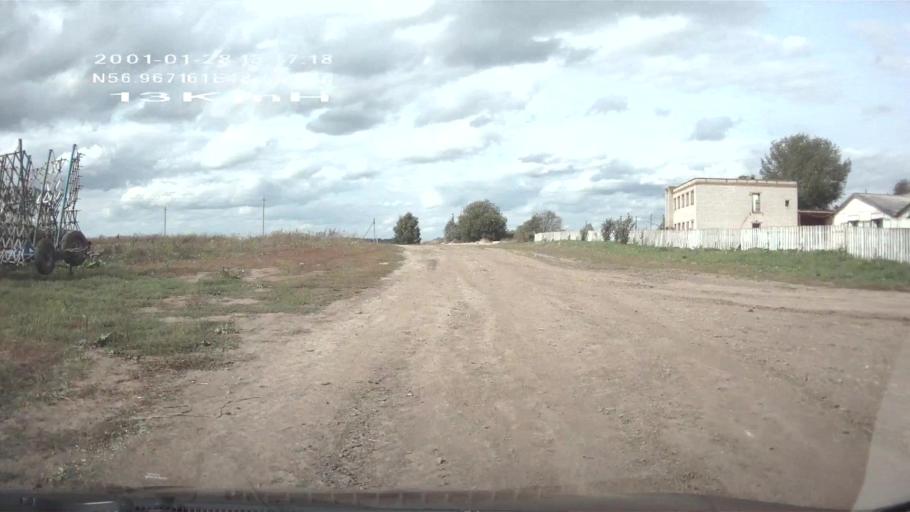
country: RU
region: Mariy-El
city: Kuzhener
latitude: 56.9672
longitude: 48.7860
